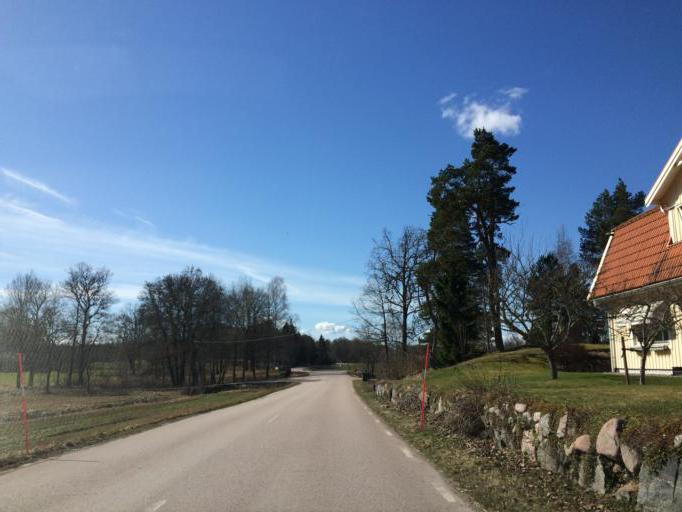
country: SE
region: Vaestmanland
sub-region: Hallstahammars Kommun
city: Kolback
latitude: 59.5249
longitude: 16.3115
